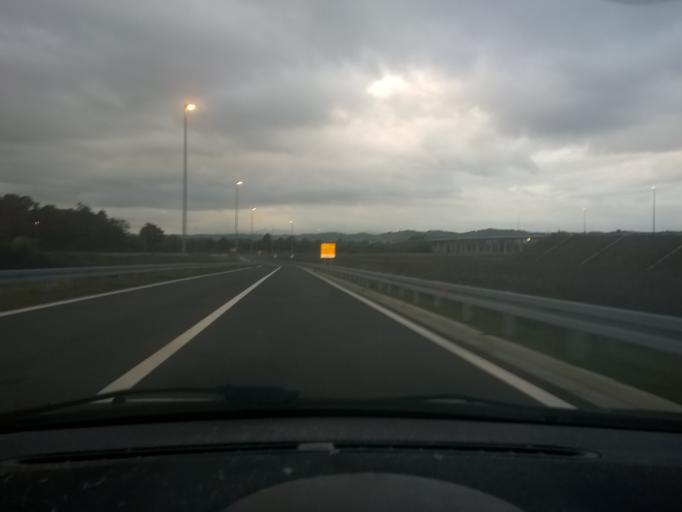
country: HR
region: Krapinsko-Zagorska
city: Oroslavje
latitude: 46.0129
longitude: 15.9335
